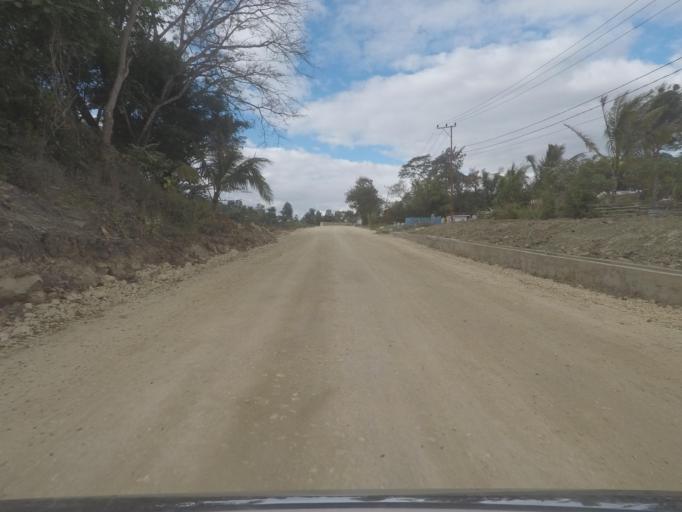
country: TL
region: Baucau
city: Venilale
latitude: -8.6410
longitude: 126.3768
